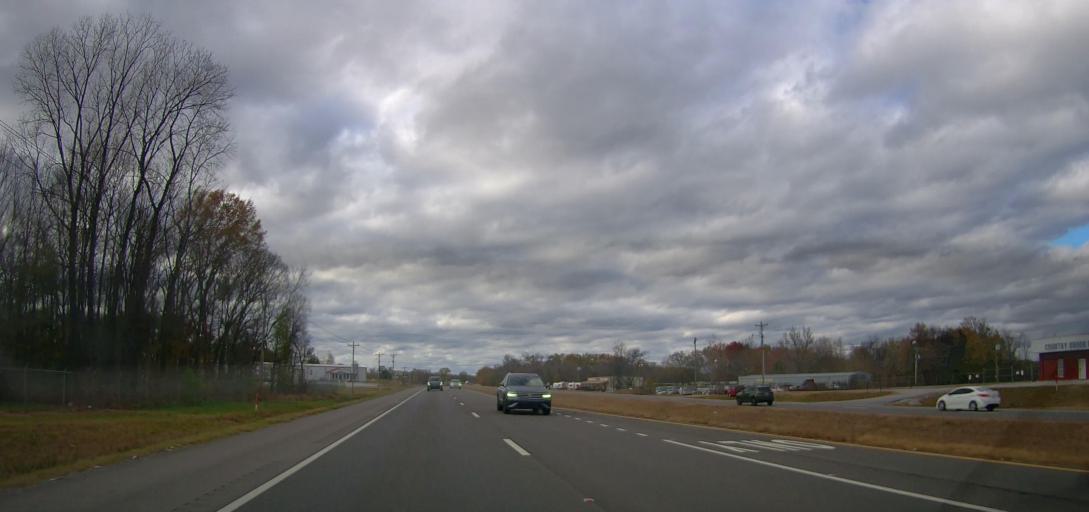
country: US
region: Alabama
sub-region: Lawrence County
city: Moulton
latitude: 34.4642
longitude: -87.2543
